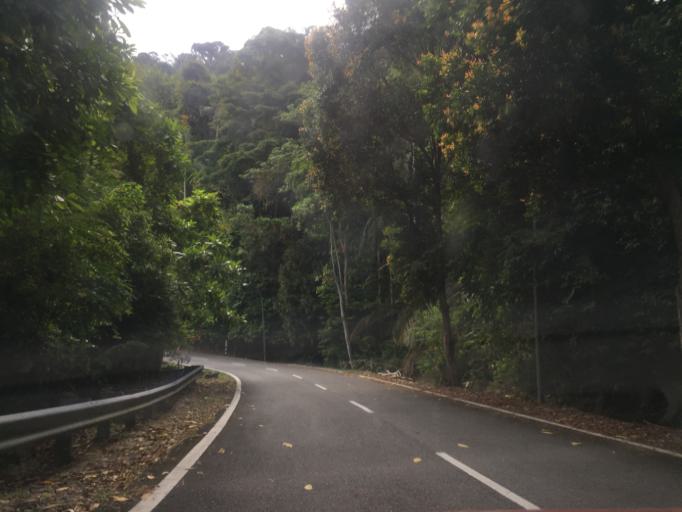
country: MY
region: Perak
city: Lumut
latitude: 4.2471
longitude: 100.5602
